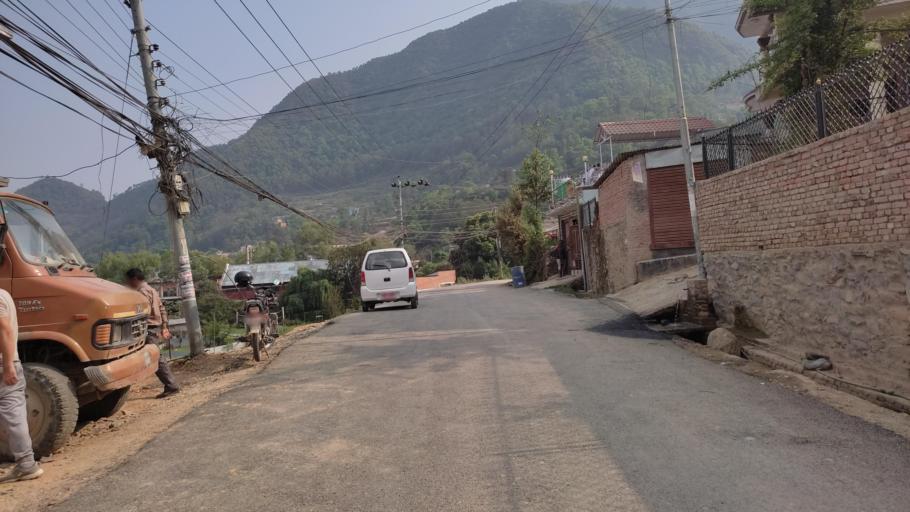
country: NP
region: Central Region
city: Kirtipur
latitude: 27.6649
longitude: 85.2583
